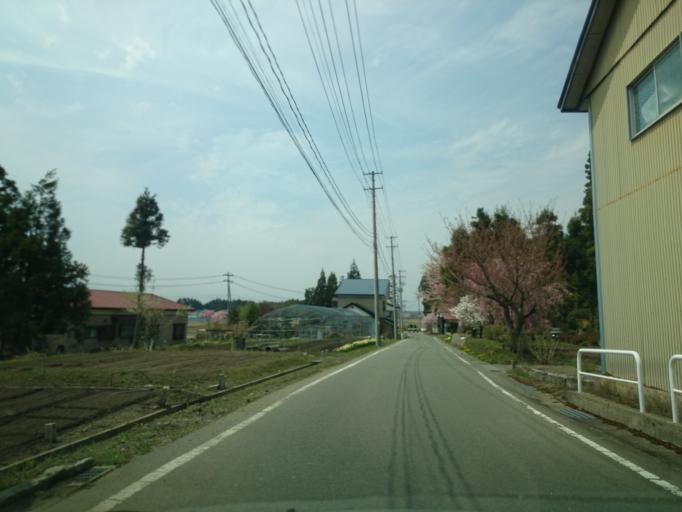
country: JP
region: Fukushima
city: Inawashiro
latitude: 37.5570
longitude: 140.1365
